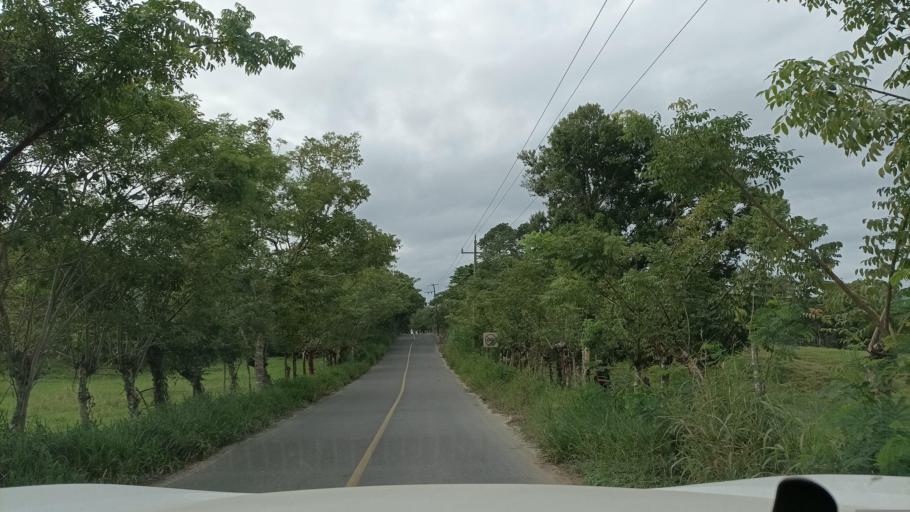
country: MX
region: Veracruz
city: Hidalgotitlan
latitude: 17.6979
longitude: -94.4685
